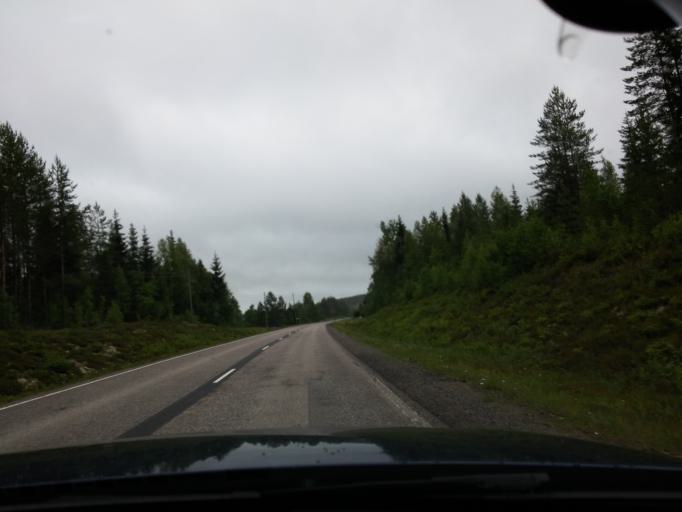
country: FI
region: Central Finland
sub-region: Keuruu
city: Keuruu
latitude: 62.3397
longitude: 24.7348
